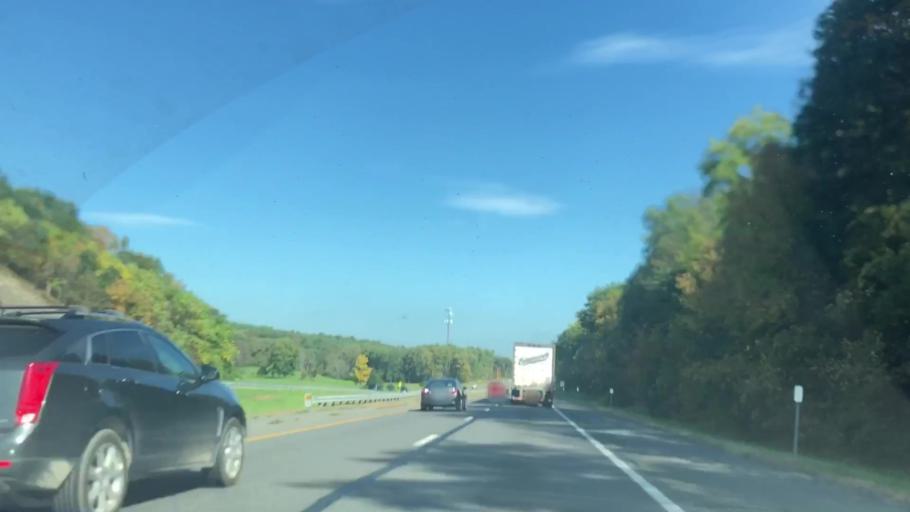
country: US
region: New York
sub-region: Greene County
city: Coxsackie
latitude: 42.3223
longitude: -73.8648
